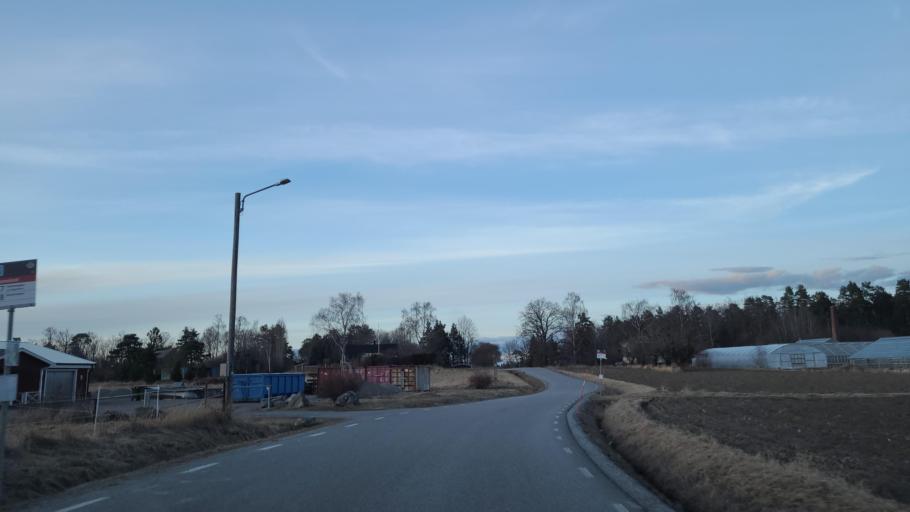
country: SE
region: Stockholm
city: Stenhamra
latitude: 59.4068
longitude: 17.6598
